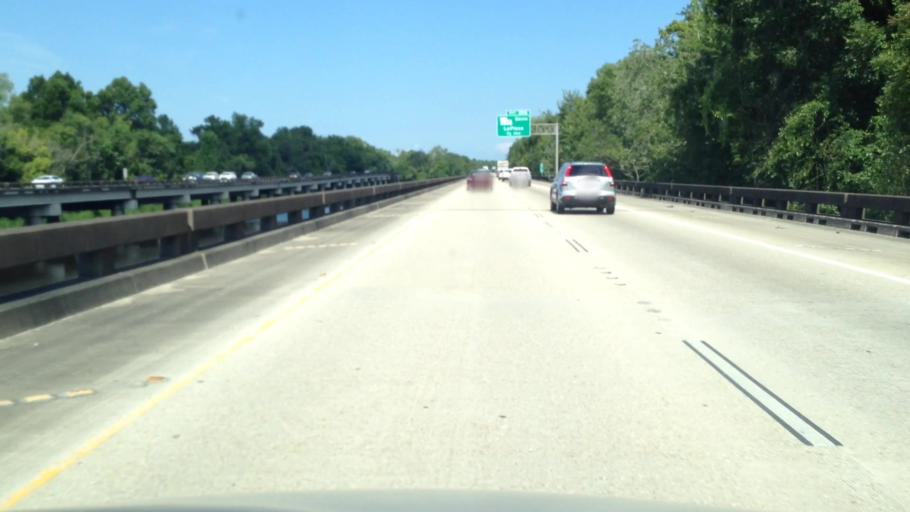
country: US
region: Louisiana
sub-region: Saint John the Baptist Parish
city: Montegut
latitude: 30.1080
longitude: -90.5136
